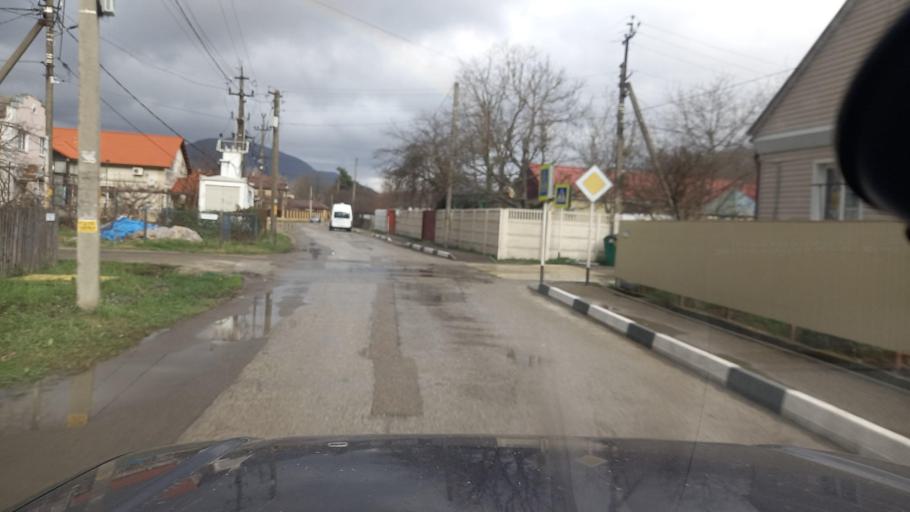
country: RU
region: Krasnodarskiy
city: Pshada
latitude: 44.4732
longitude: 38.3975
